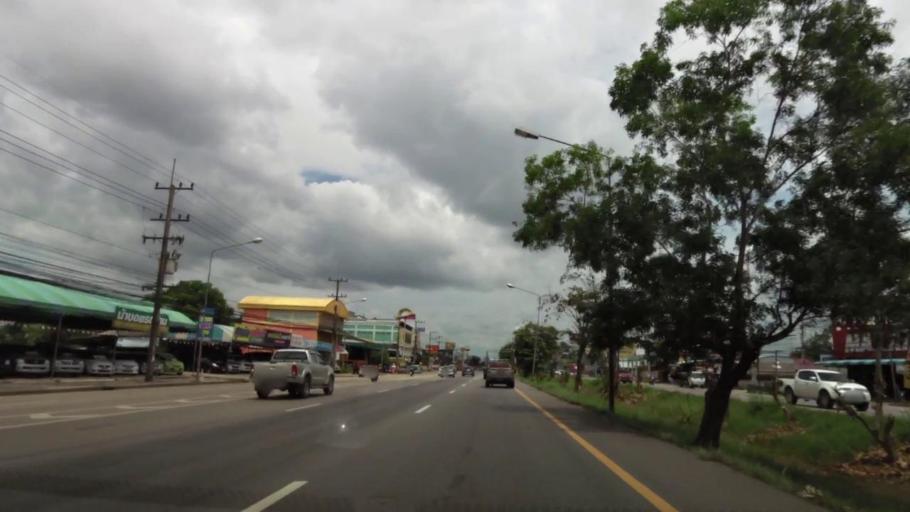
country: TH
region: Rayong
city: Klaeng
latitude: 12.7865
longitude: 101.6686
